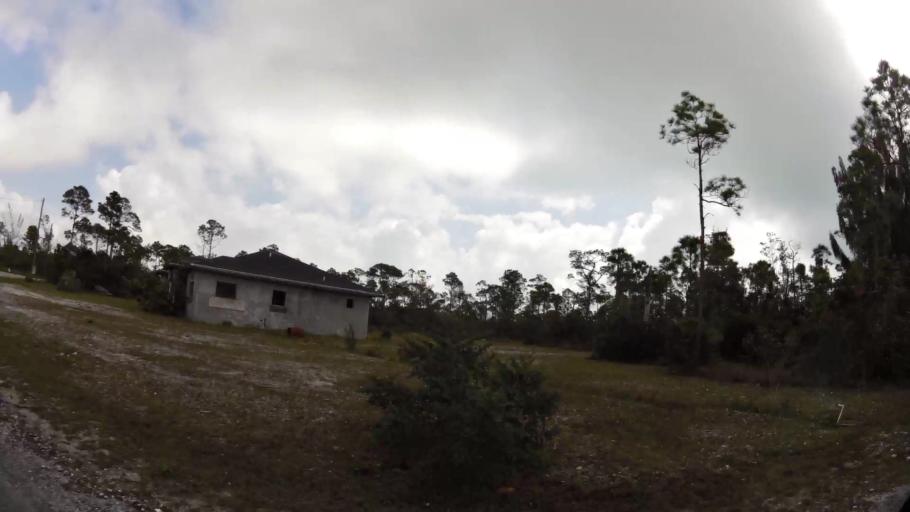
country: BS
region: Freeport
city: Lucaya
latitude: 26.5340
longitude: -78.6039
